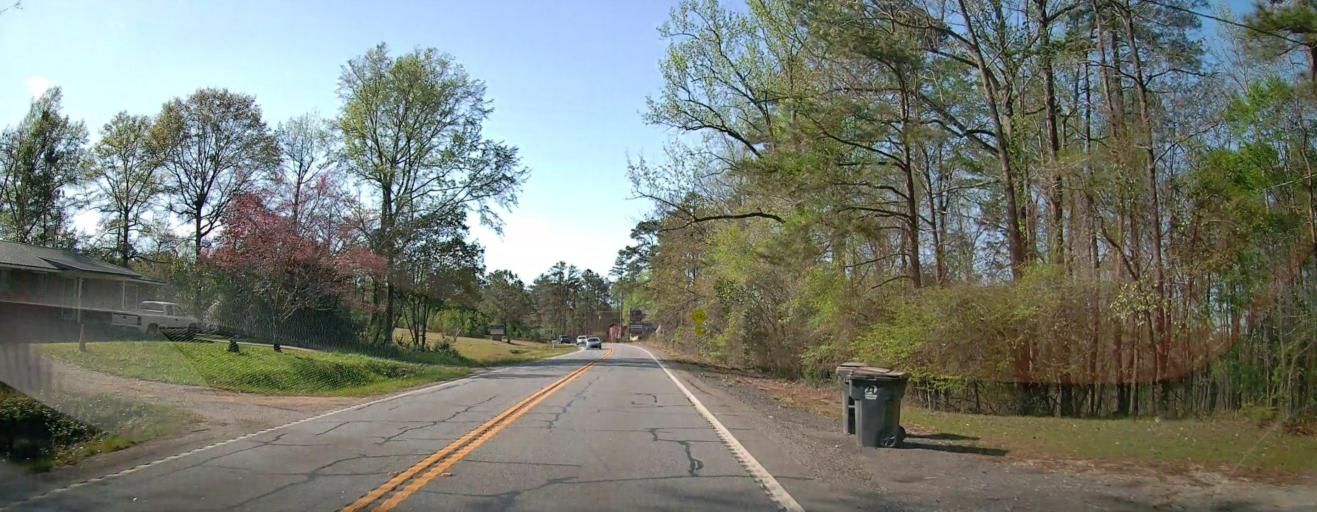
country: US
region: Georgia
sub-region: Baldwin County
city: Hardwick
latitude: 33.0878
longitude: -83.1729
